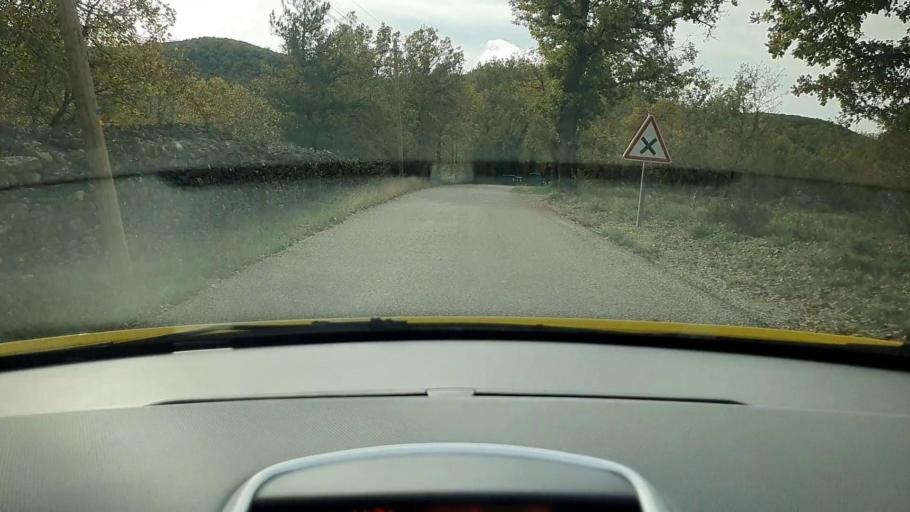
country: FR
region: Languedoc-Roussillon
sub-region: Departement du Gard
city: Lasalle
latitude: 44.0408
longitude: 3.9119
